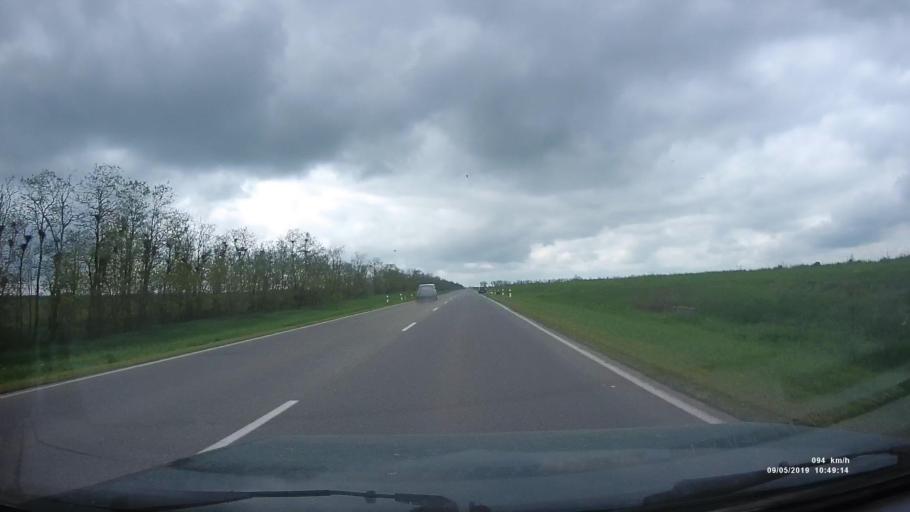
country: RU
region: Rostov
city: Peshkovo
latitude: 46.9453
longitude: 39.3555
